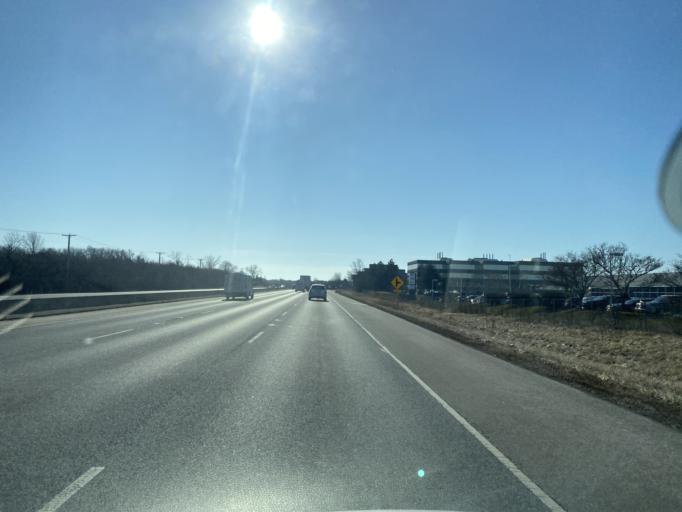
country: US
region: Illinois
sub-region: DuPage County
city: Clarendon Hills
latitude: 41.8232
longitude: -87.9535
